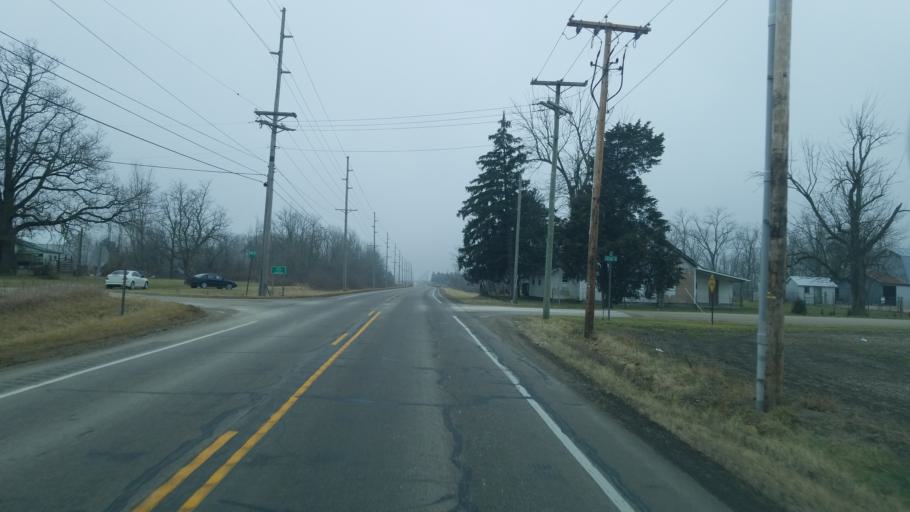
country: US
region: Indiana
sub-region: Adams County
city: Geneva
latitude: 40.5712
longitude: -84.9595
